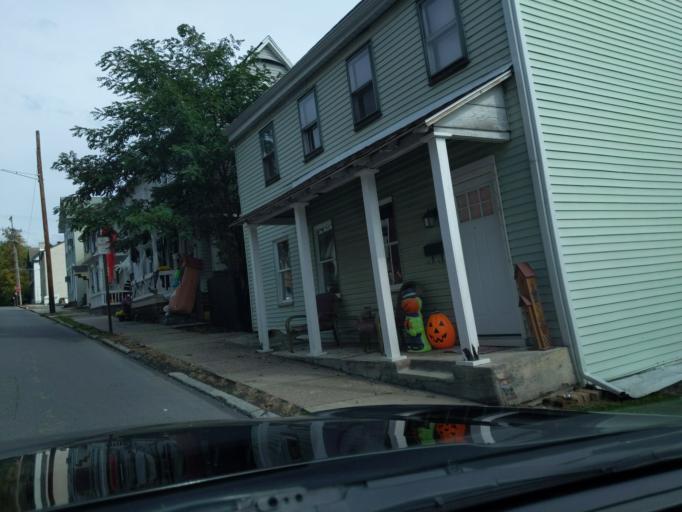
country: US
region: Pennsylvania
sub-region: Blair County
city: Hollidaysburg
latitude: 40.4296
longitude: -78.3963
